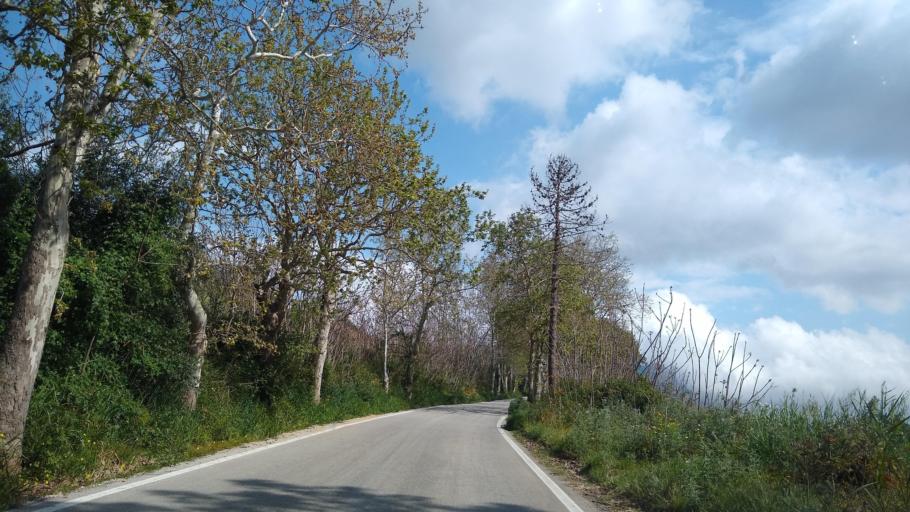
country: IT
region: Sicily
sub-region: Trapani
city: Calatafimi
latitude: 37.9386
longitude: 12.8509
